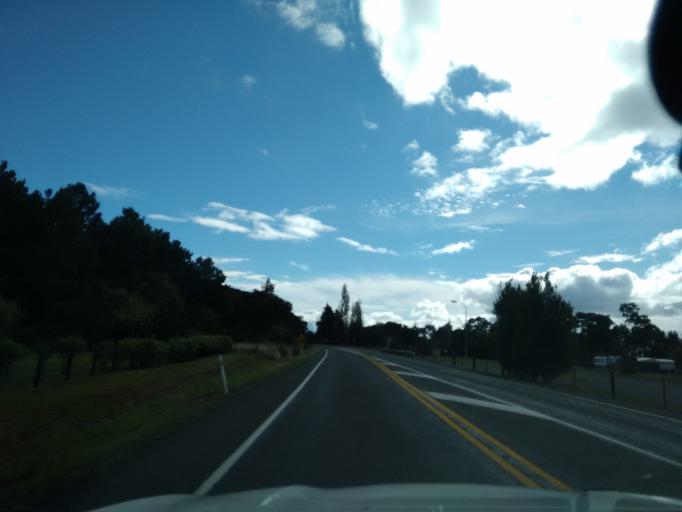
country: NZ
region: Waikato
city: Turangi
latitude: -38.8872
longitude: 175.9568
